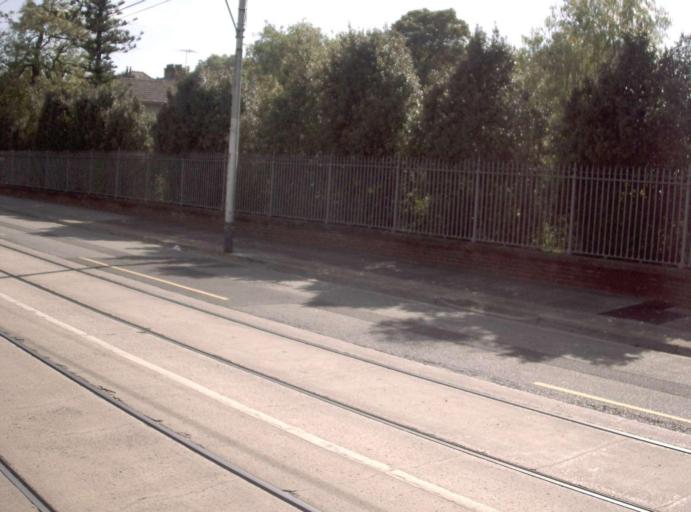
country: AU
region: Victoria
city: Toorak
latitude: -37.8487
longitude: 145.0305
